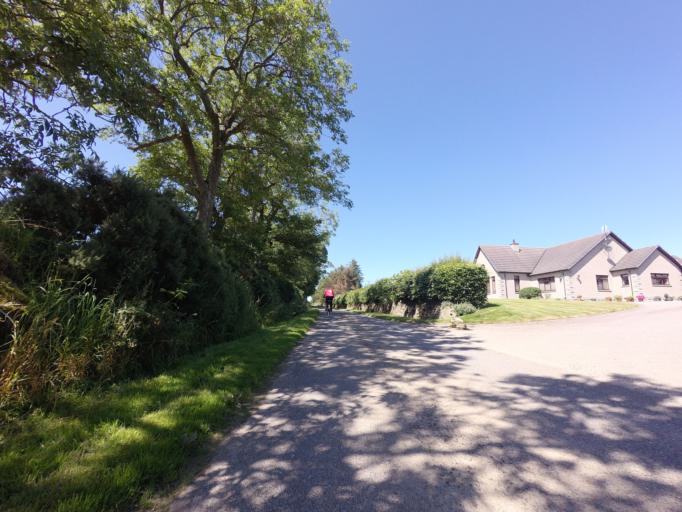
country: GB
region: Scotland
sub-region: Aberdeenshire
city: Macduff
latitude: 57.6377
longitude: -2.4934
